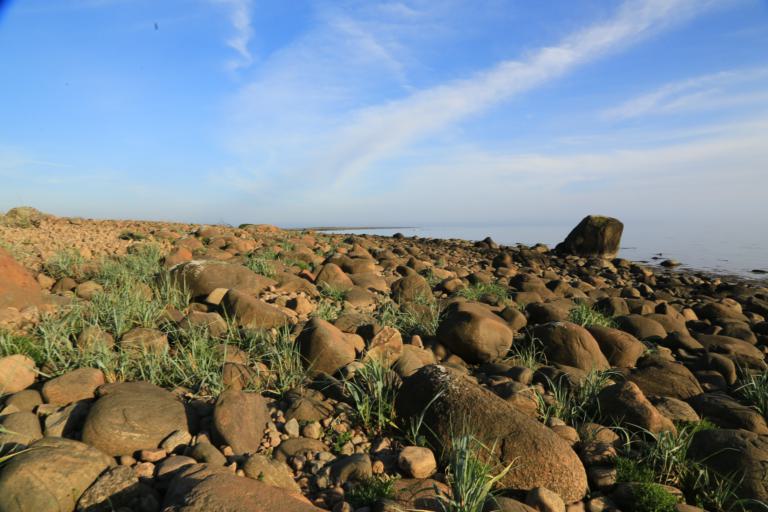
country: SE
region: Halland
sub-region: Varbergs Kommun
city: Traslovslage
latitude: 57.0381
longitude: 12.2936
